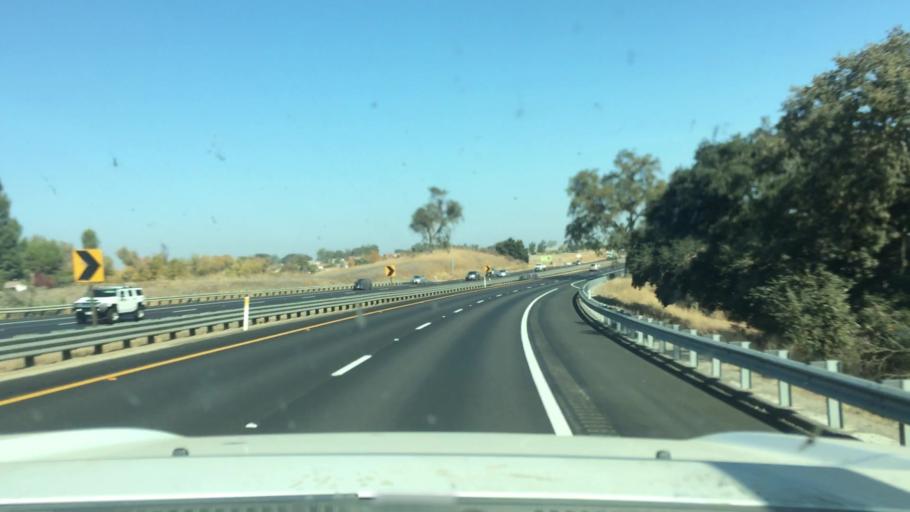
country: US
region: California
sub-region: San Luis Obispo County
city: Templeton
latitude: 35.5744
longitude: -120.7050
